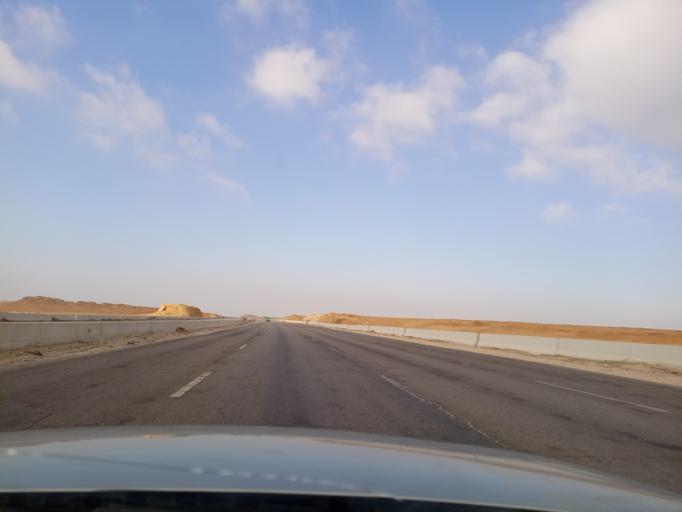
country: EG
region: Al Jizah
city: Al `Ayyat
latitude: 29.6704
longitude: 31.1888
